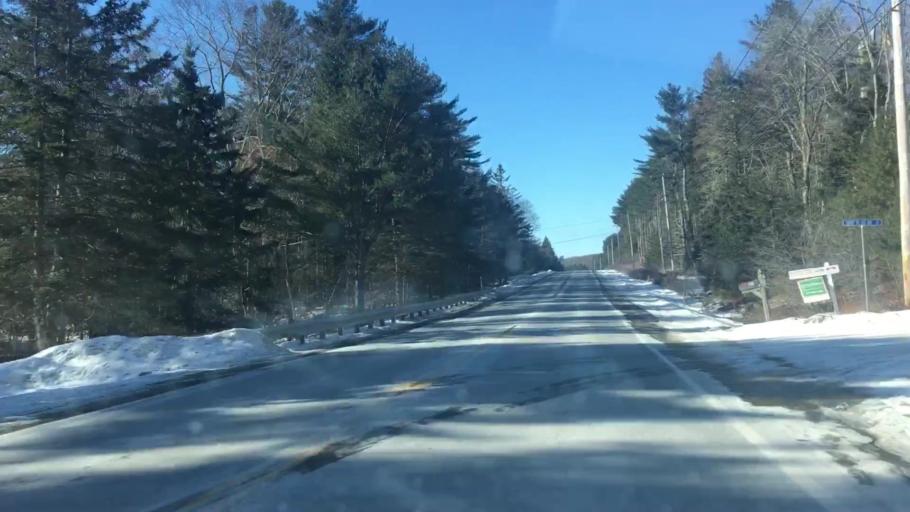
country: US
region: Maine
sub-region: Hancock County
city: Surry
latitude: 44.4952
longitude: -68.4800
